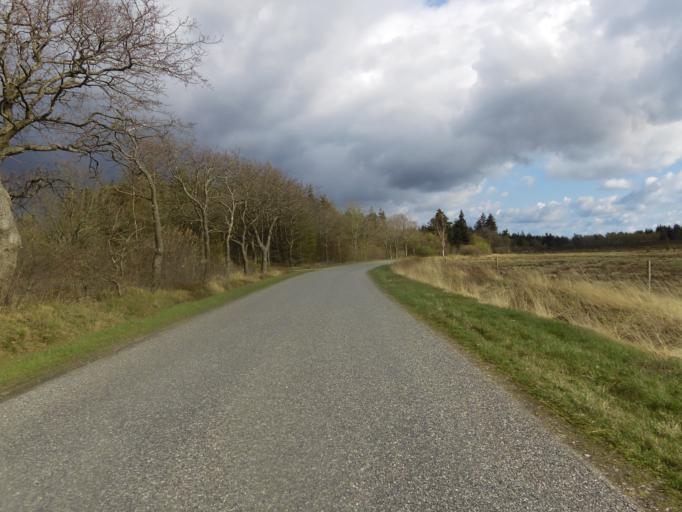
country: DK
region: South Denmark
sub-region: Haderslev Kommune
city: Gram
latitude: 55.2721
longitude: 8.9490
